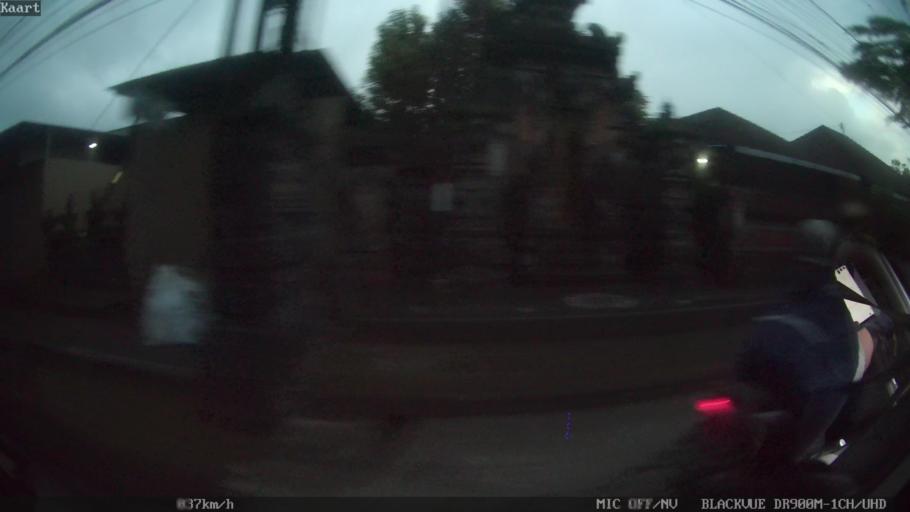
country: ID
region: Bali
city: Banjar Parekan
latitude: -8.5725
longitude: 115.2189
